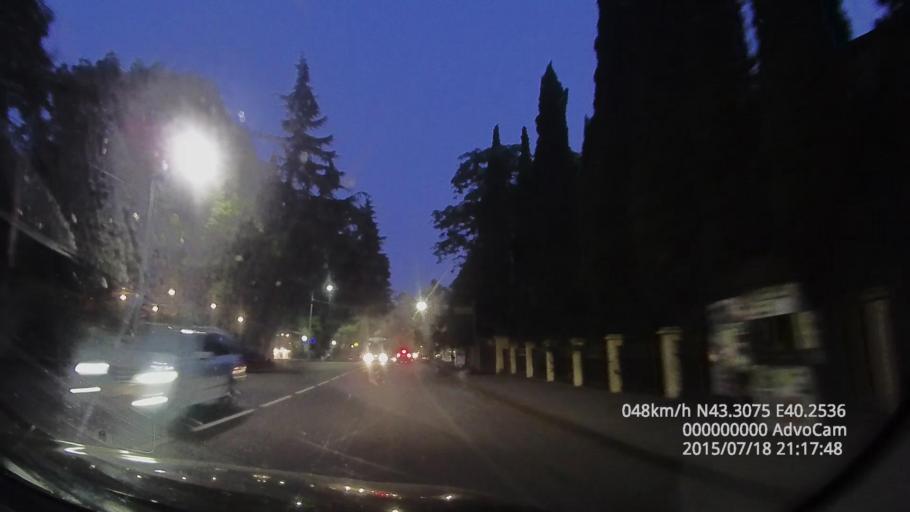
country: GE
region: Abkhazia
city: Gagra
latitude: 43.3072
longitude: 40.2537
